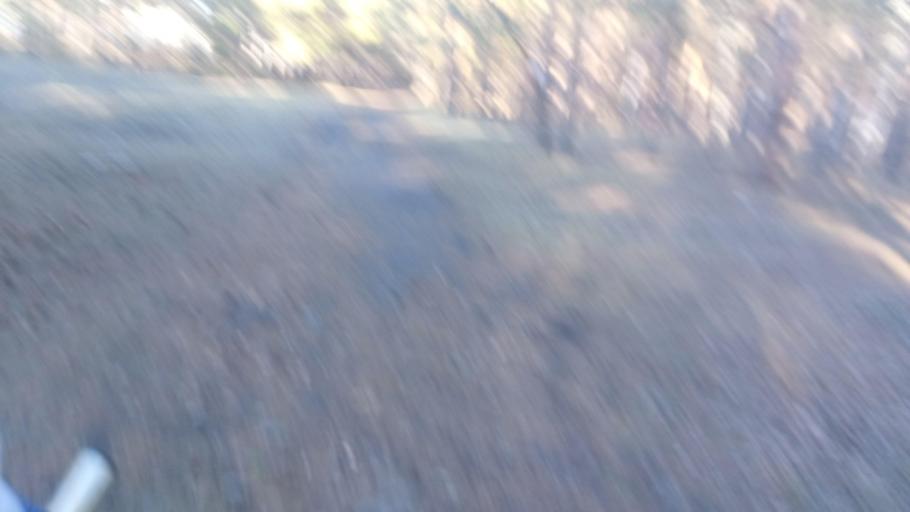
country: RU
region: Chelyabinsk
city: Novosineglazovskiy
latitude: 55.1261
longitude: 61.3323
